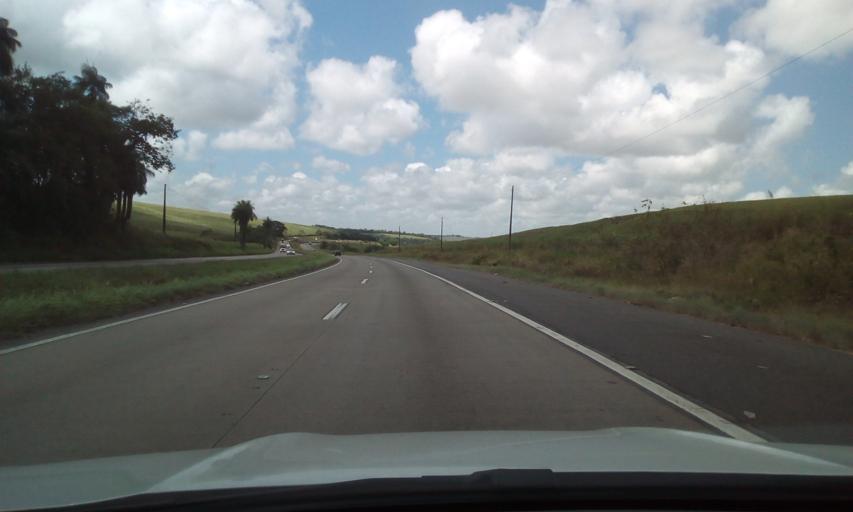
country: BR
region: Pernambuco
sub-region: Itapissuma
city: Itapissuma
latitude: -7.7809
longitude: -34.9317
